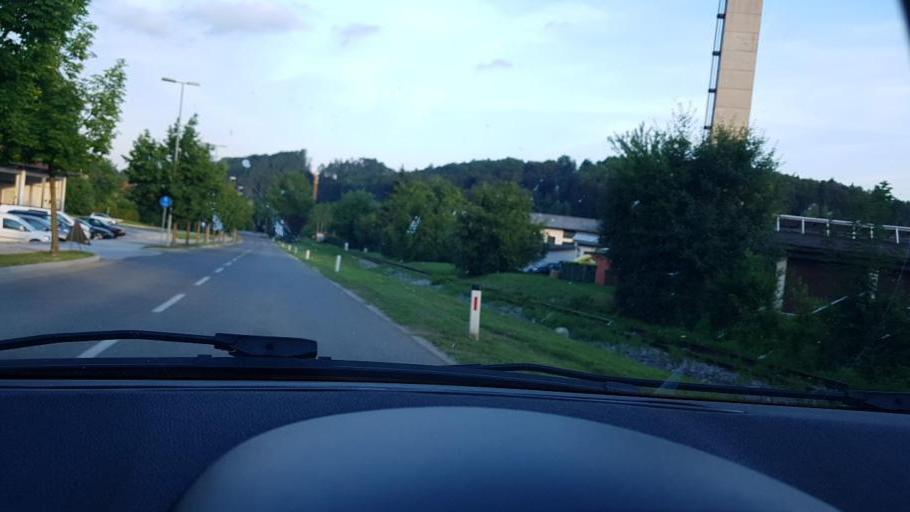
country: SI
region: Rogaska Slatina
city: Rogaska Slatina
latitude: 46.2422
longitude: 15.6274
